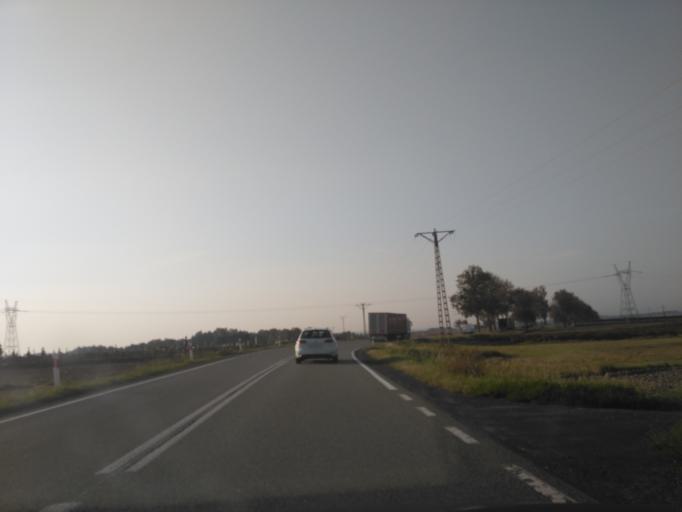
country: PL
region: Lublin Voivodeship
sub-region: Powiat krasnicki
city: Szastarka
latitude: 50.8167
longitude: 22.3185
